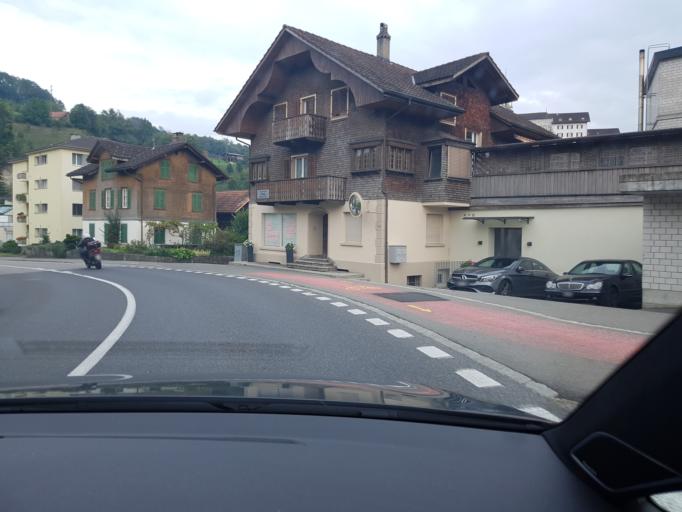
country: CH
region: Lucerne
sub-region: Entlebuch District
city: Werthenstein
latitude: 47.0556
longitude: 8.1005
